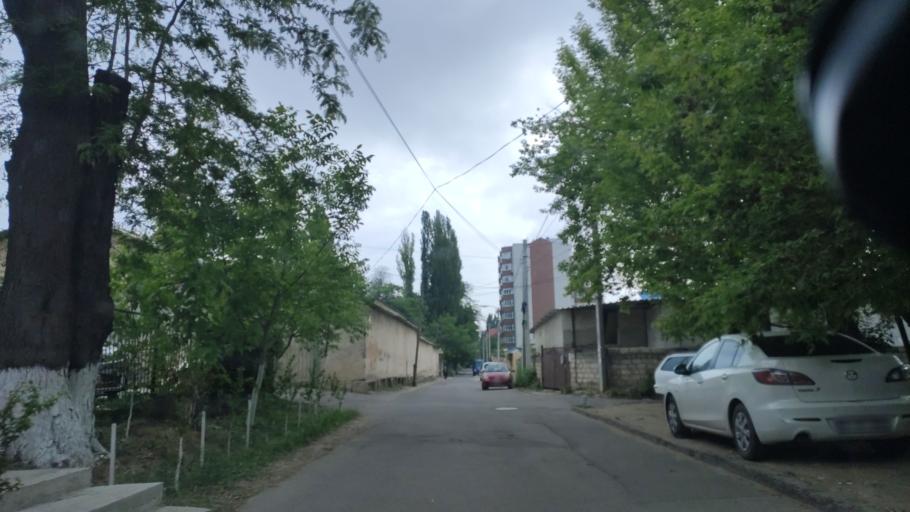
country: MD
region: Chisinau
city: Chisinau
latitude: 46.9838
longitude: 28.8706
